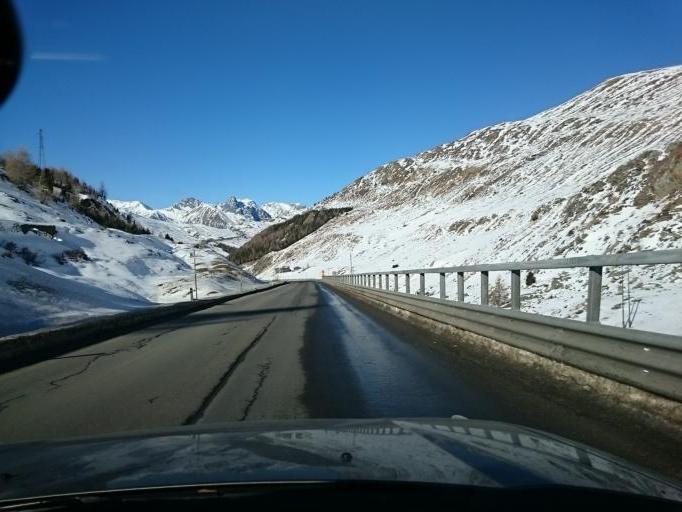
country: IT
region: Lombardy
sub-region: Provincia di Sondrio
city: Livigno
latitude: 46.5113
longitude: 10.1958
